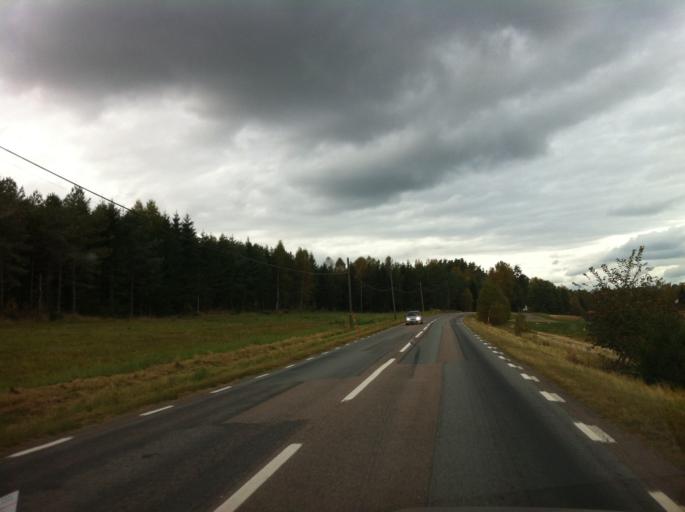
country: SE
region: OEstergoetland
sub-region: Motala Kommun
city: Motala
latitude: 58.6114
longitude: 14.9841
